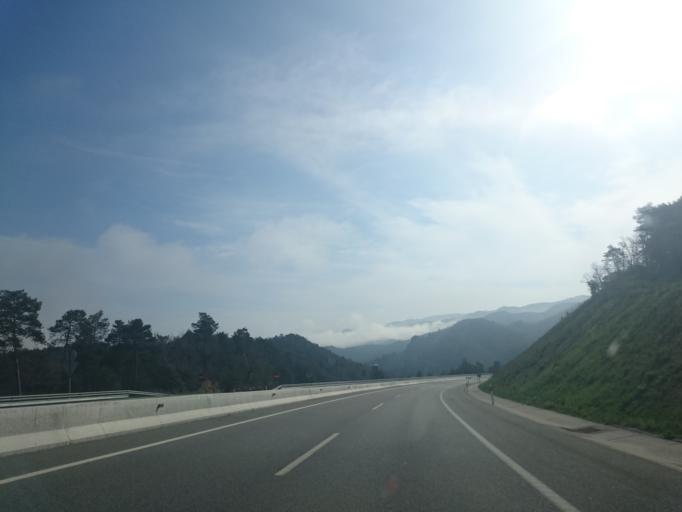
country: ES
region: Catalonia
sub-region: Provincia de Barcelona
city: Sant Julia de Vilatorta
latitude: 41.8952
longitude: 2.3668
